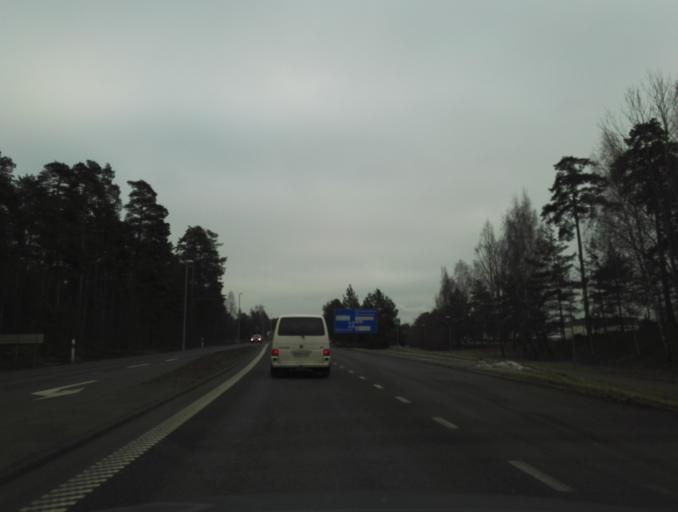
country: SE
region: Kronoberg
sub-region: Vaxjo Kommun
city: Vaexjoe
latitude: 56.8831
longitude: 14.8307
